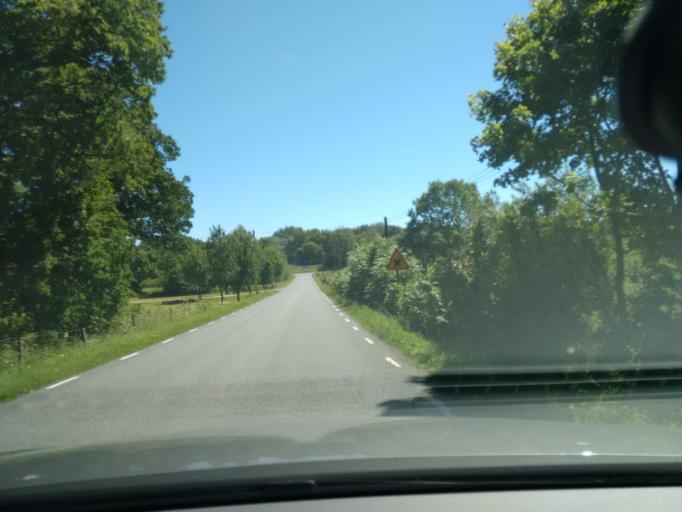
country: SE
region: Skane
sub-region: Kristianstads Kommun
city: Degeberga
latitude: 55.7682
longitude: 13.9992
